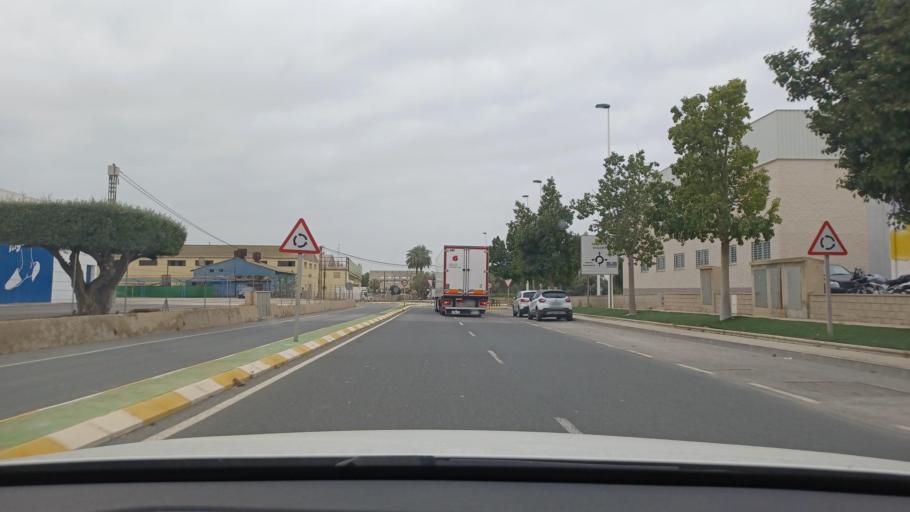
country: ES
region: Valencia
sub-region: Provincia de Alicante
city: Elche
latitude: 38.2458
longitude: -0.7060
